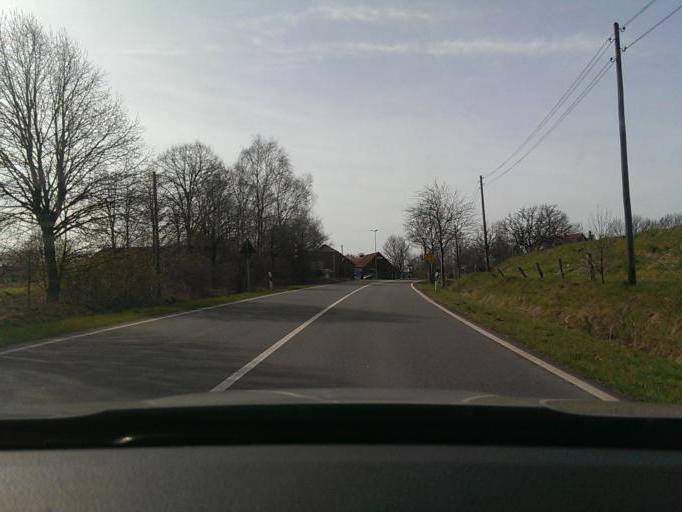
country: DE
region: Lower Saxony
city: Garbsen-Mitte
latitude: 52.5071
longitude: 9.6316
